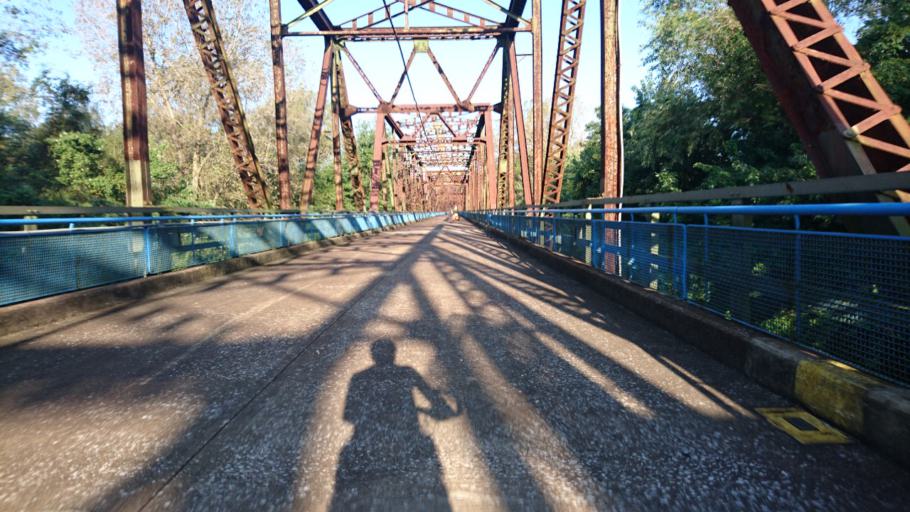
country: US
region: Missouri
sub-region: Saint Louis County
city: Glasgow Village
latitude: 38.7573
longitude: -90.1655
